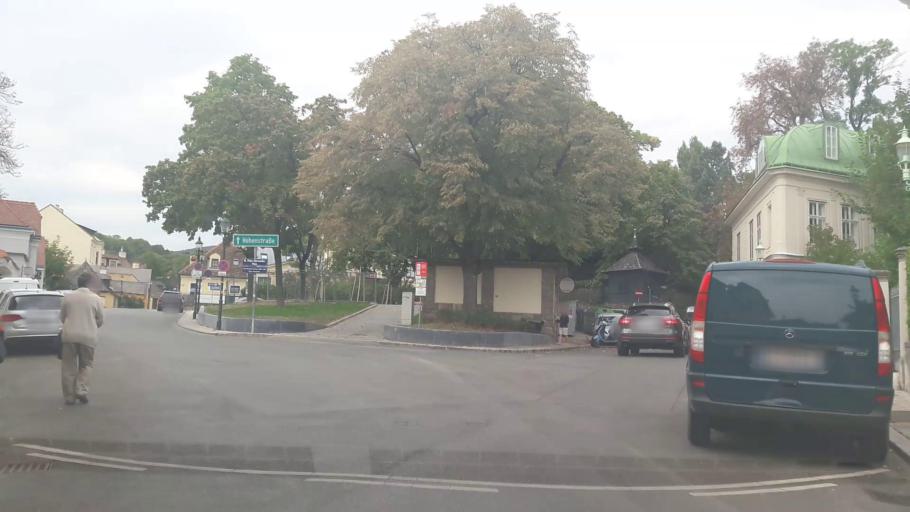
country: AT
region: Lower Austria
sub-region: Politischer Bezirk Korneuburg
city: Langenzersdorf
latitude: 48.2578
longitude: 16.3382
